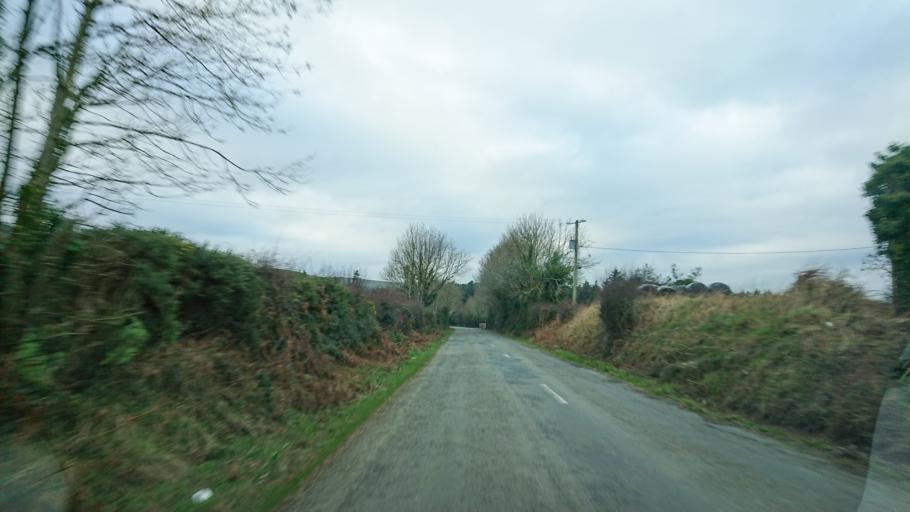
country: IE
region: Munster
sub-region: South Tipperary
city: Cluain Meala
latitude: 52.3228
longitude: -7.5727
